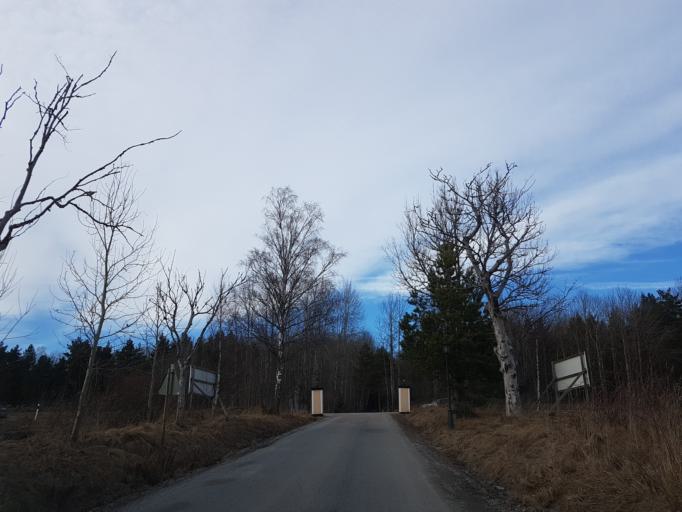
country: SE
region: Stockholm
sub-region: Norrtalje Kommun
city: Nykvarn
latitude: 59.7395
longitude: 18.1910
